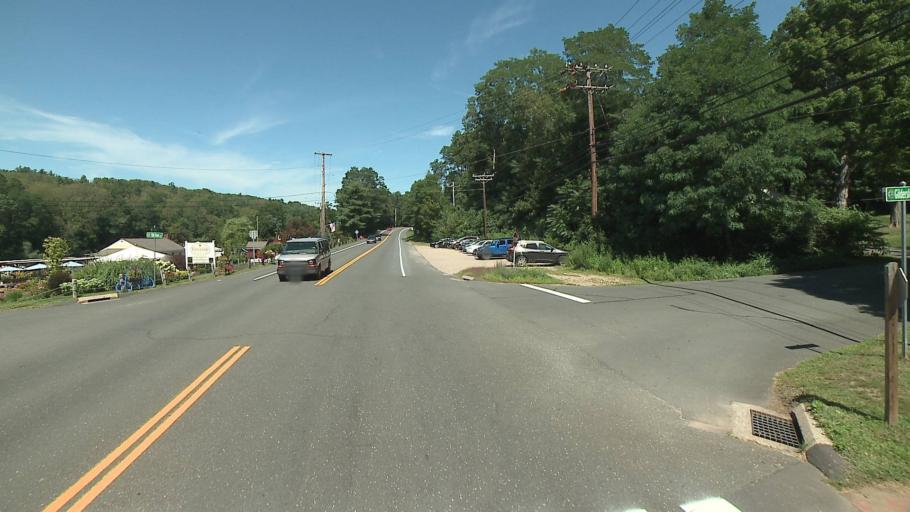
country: US
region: Connecticut
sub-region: Hartford County
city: Collinsville
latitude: 41.8200
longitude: -72.9220
